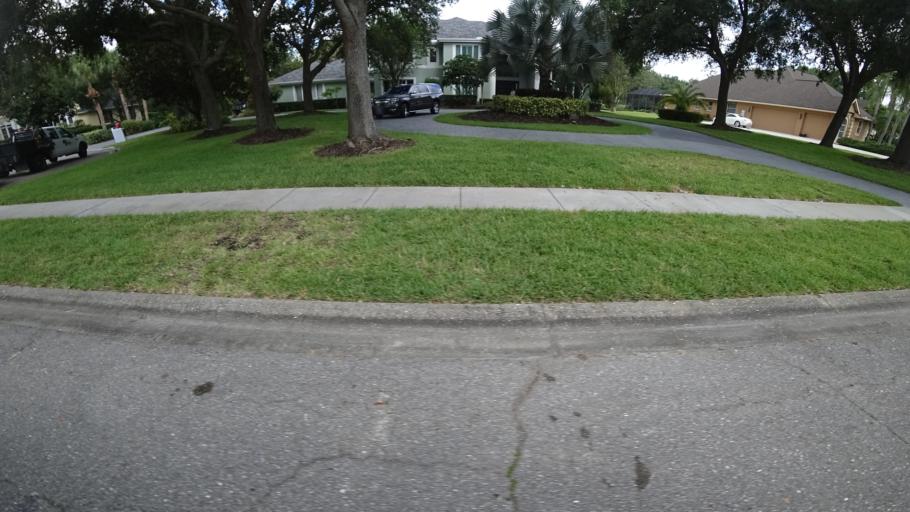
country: US
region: Florida
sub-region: Sarasota County
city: The Meadows
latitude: 27.4185
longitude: -82.4328
